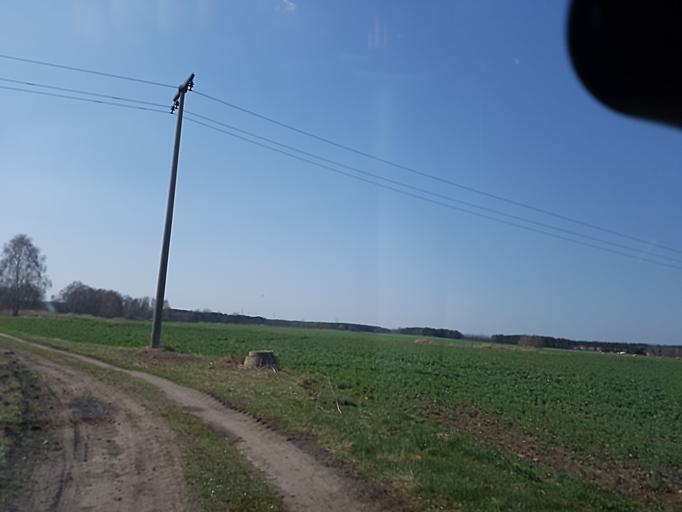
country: DE
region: Brandenburg
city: Trobitz
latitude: 51.5684
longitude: 13.4129
